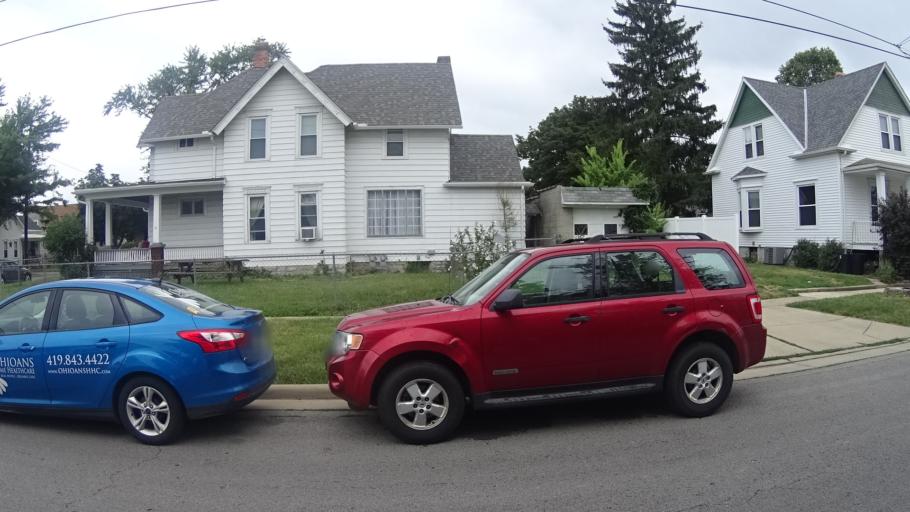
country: US
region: Ohio
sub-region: Erie County
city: Sandusky
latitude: 41.4503
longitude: -82.6988
